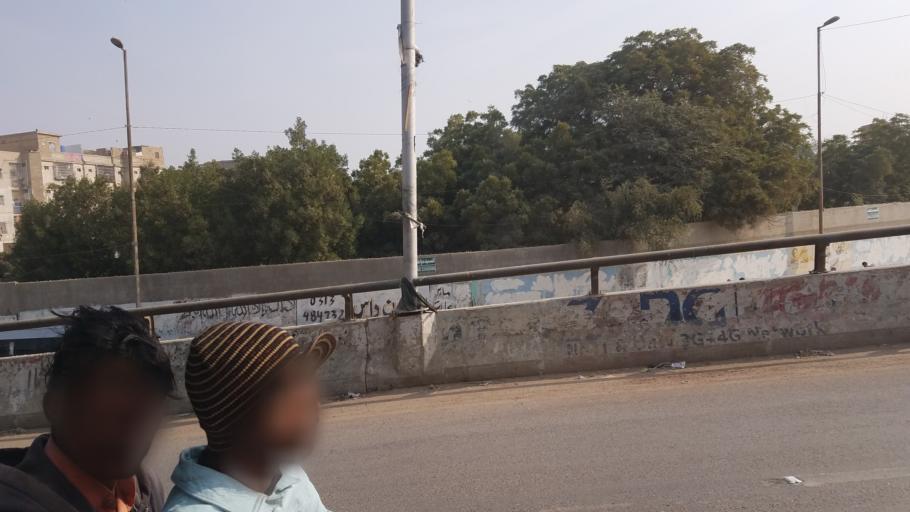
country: PK
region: Sindh
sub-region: Karachi District
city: Karachi
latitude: 24.9453
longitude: 67.0838
